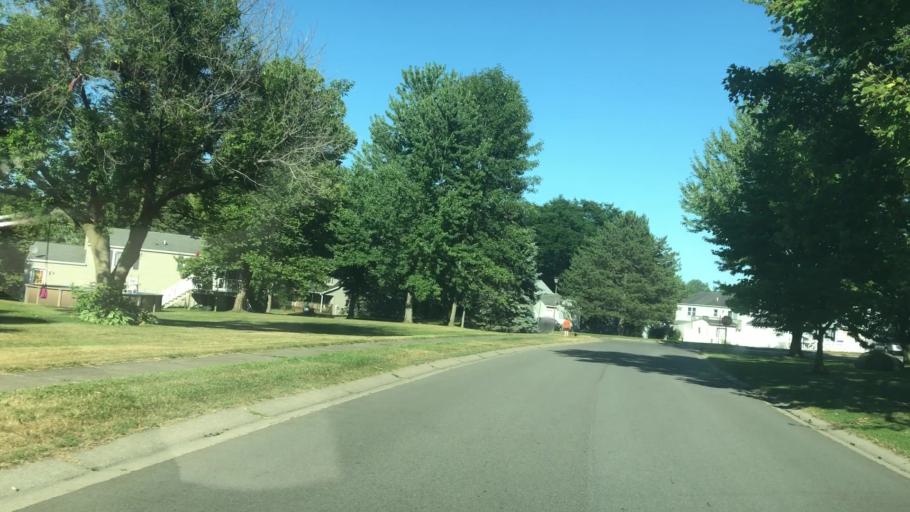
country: US
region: New York
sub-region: Wayne County
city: Macedon
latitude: 43.1278
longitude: -77.3084
